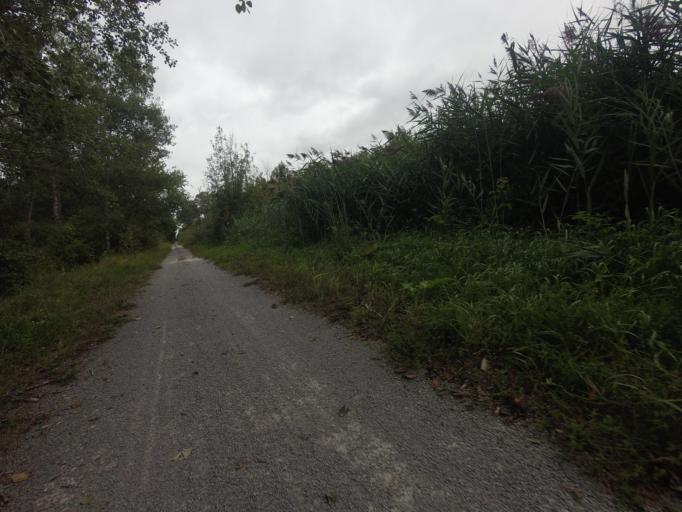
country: CA
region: Ontario
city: Uxbridge
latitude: 44.2979
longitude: -78.9494
